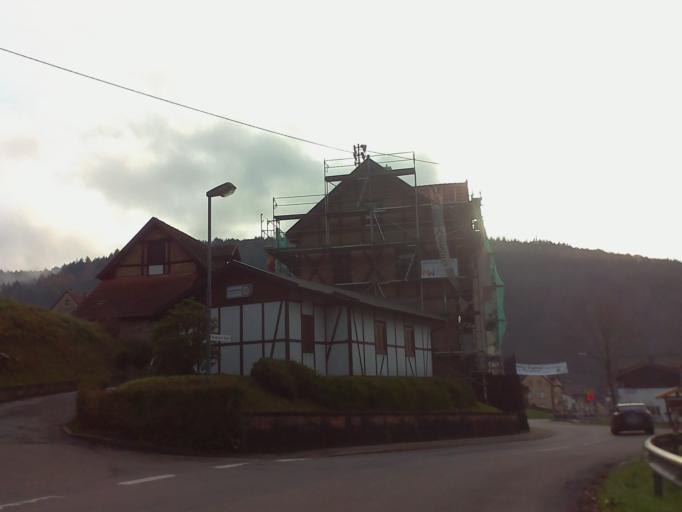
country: DE
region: Baden-Wuerttemberg
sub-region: Karlsruhe Region
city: Heiligkreuzsteinach
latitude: 49.4876
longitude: 8.7949
